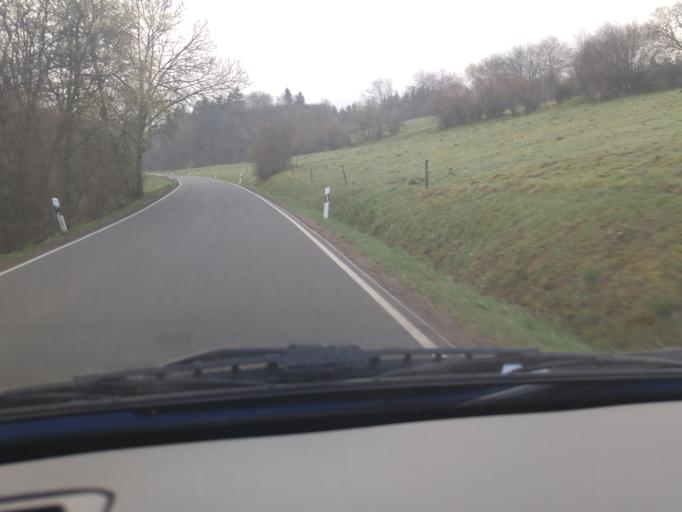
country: DE
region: Hesse
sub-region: Regierungsbezirk Giessen
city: Ulrichstein
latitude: 50.5297
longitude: 9.1855
